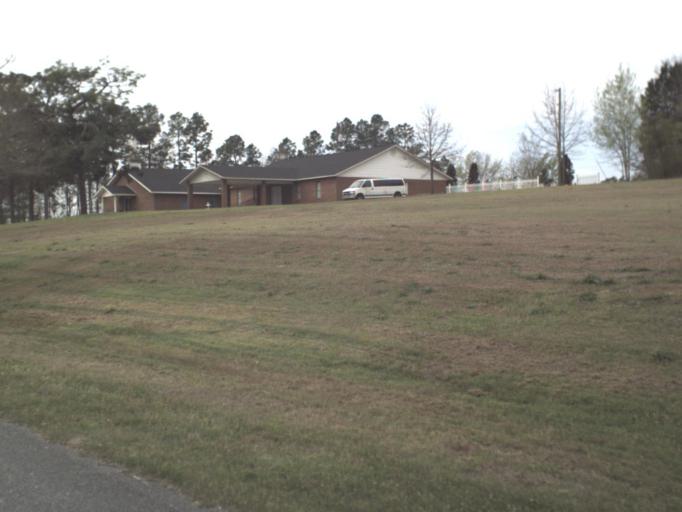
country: US
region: Florida
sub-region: Jackson County
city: Graceville
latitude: 30.9336
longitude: -85.6491
